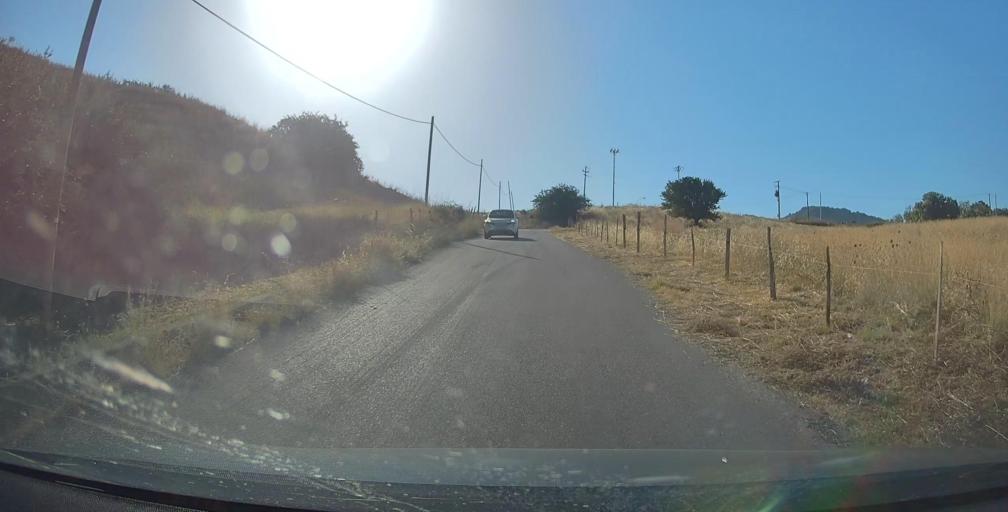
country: IT
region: Sicily
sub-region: Messina
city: San Piero Patti
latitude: 38.0757
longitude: 14.9818
